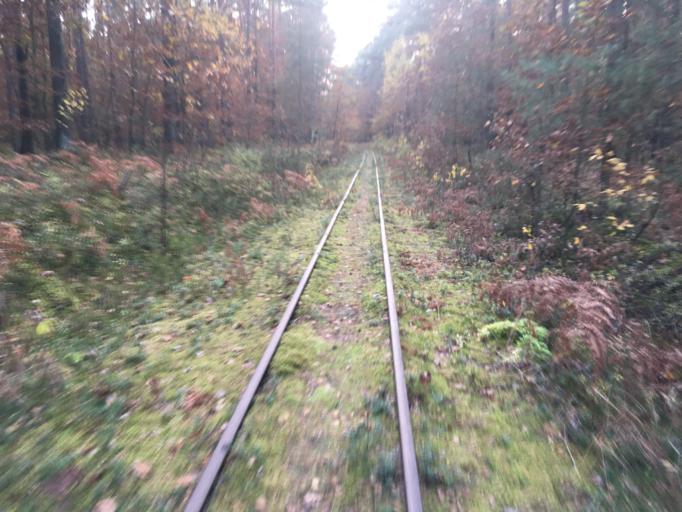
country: PL
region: Swietokrzyskie
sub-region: Powiat starachowicki
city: Starachowice
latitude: 51.0700
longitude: 21.1426
